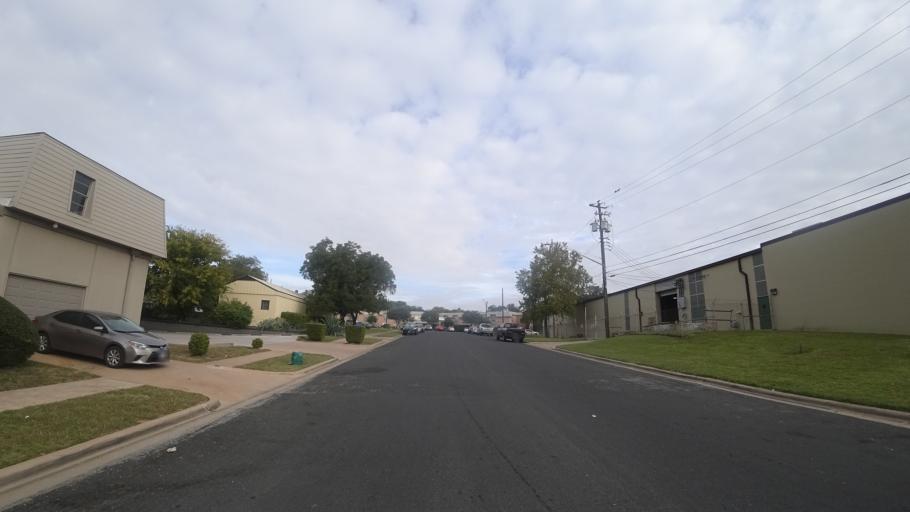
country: US
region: Texas
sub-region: Travis County
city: Austin
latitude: 30.2816
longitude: -97.7116
